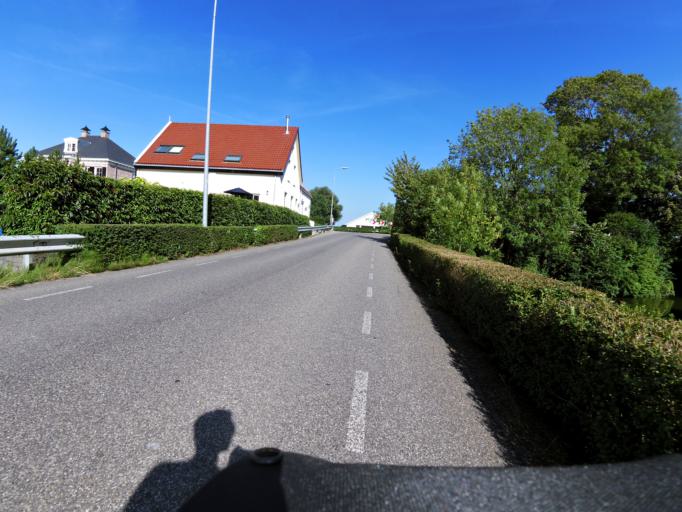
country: NL
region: South Holland
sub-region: Gemeente Goeree-Overflakkee
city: Dirksland
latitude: 51.7512
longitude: 4.1028
